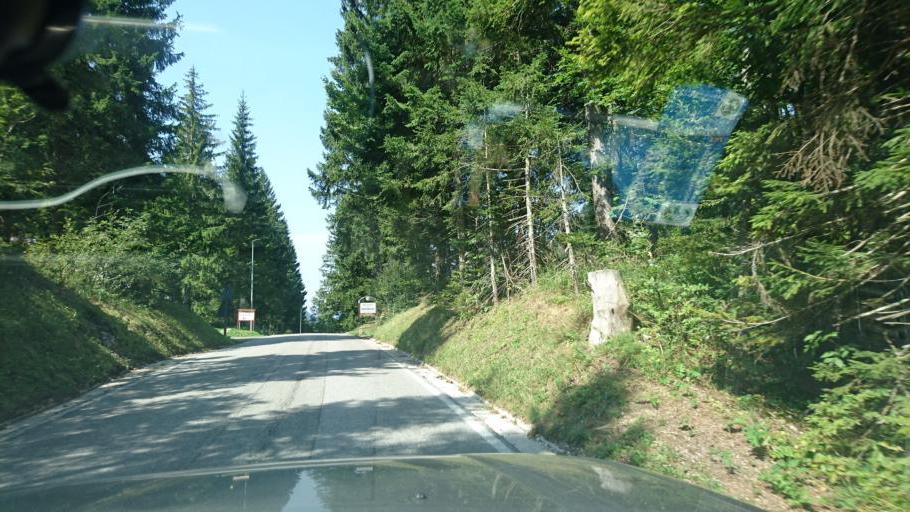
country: SI
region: Bovec
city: Bovec
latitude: 46.3902
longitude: 13.4778
